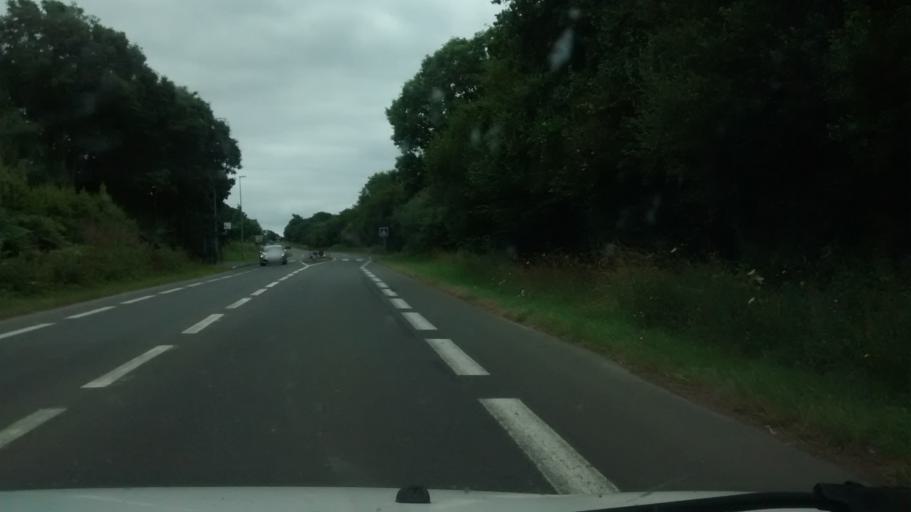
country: FR
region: Brittany
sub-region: Departement du Finistere
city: Plougastel-Daoulas
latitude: 48.3794
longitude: -4.3790
